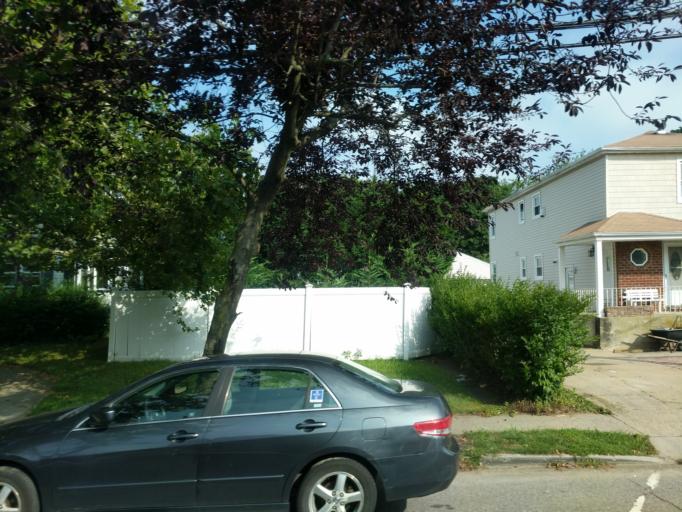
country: US
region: New York
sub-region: Nassau County
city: Lynbrook
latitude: 40.6520
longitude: -73.6805
